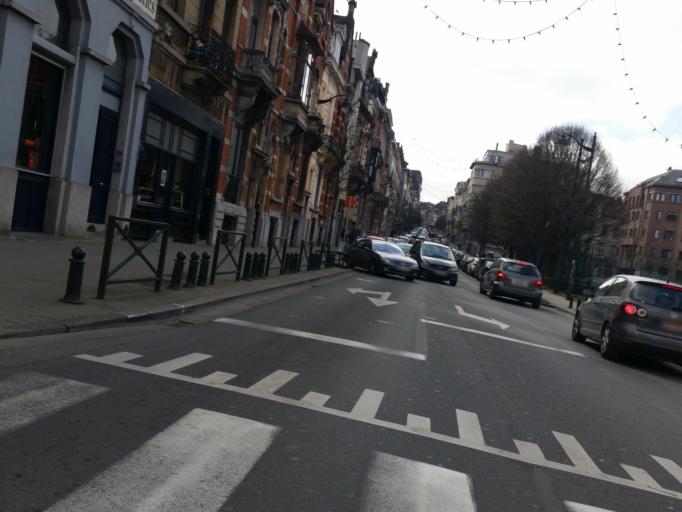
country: BE
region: Brussels Capital
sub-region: Bruxelles-Capitale
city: Brussels
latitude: 50.8306
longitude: 4.3480
